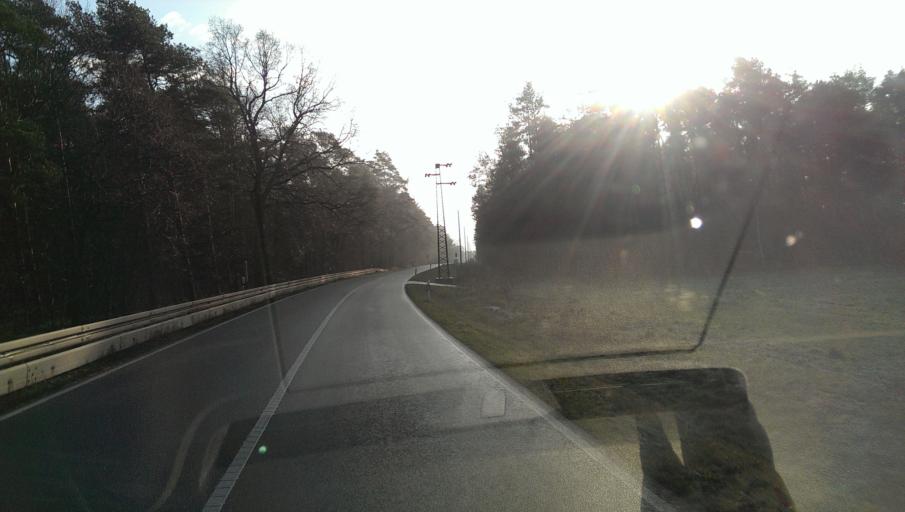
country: DE
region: Brandenburg
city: Schilda
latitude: 51.5968
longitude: 13.3553
